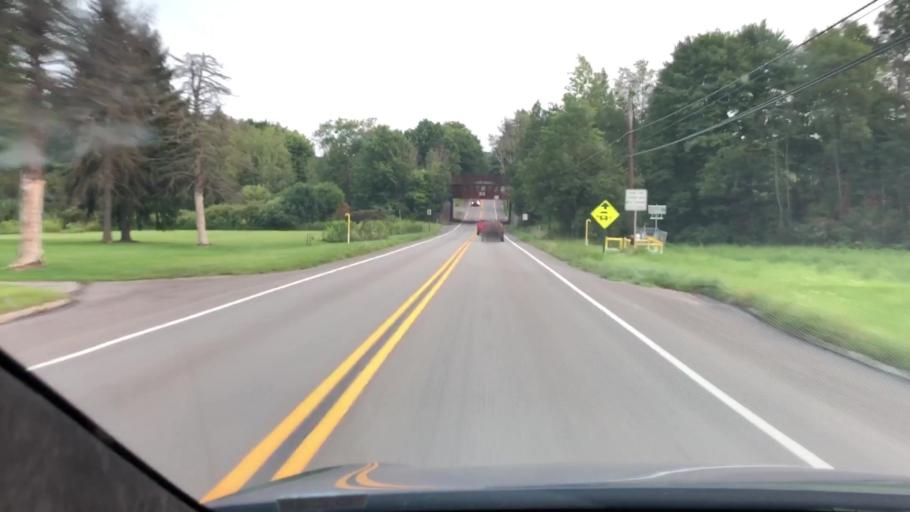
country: US
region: Pennsylvania
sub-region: Butler County
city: Slippery Rock
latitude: 41.1110
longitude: -80.0065
